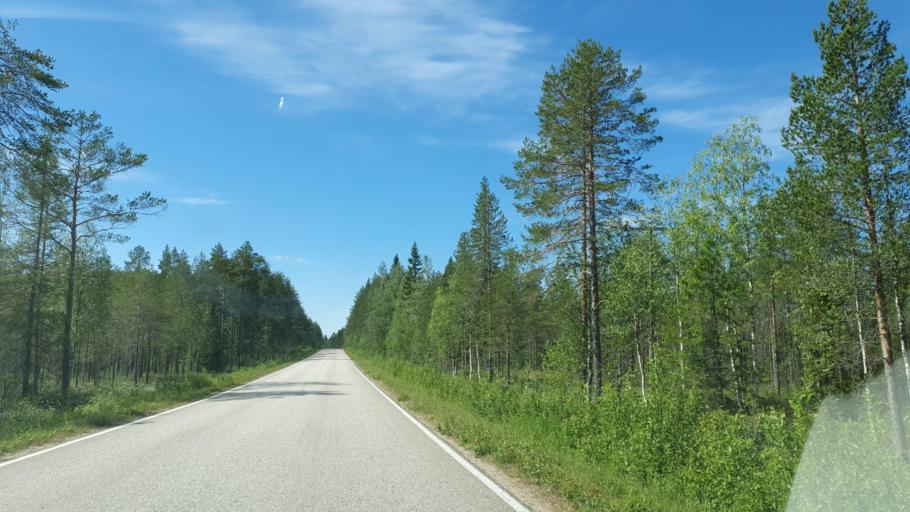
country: FI
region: Kainuu
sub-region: Kehys-Kainuu
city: Suomussalmi
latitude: 64.5819
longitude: 29.0471
